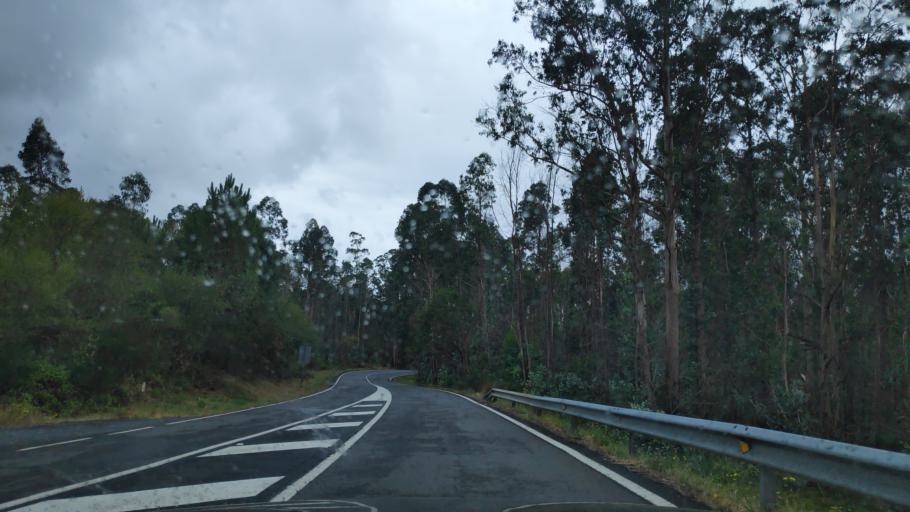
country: ES
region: Galicia
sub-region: Provincia de Pontevedra
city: Catoira
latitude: 42.6948
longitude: -8.7621
